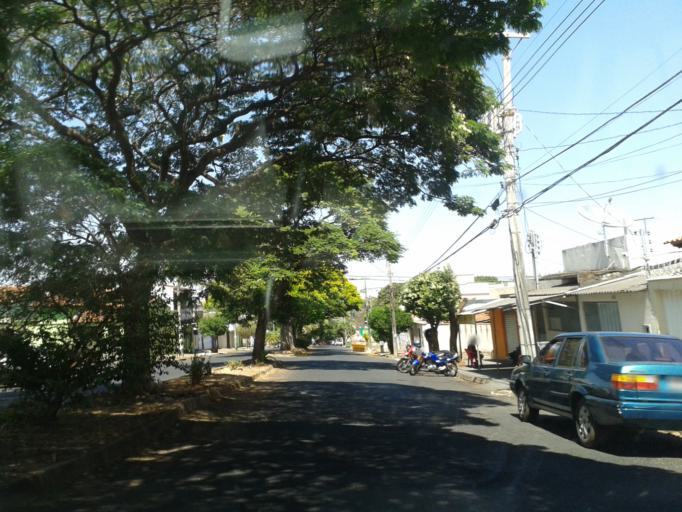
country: BR
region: Minas Gerais
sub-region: Uberlandia
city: Uberlandia
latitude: -18.9051
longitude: -48.2433
